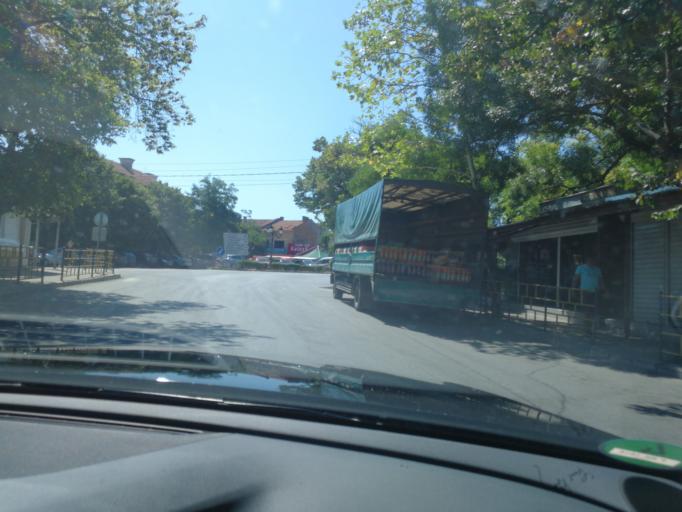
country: BG
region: Khaskovo
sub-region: Obshtina Topolovgrad
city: Topolovgrad
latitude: 42.0859
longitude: 26.3330
